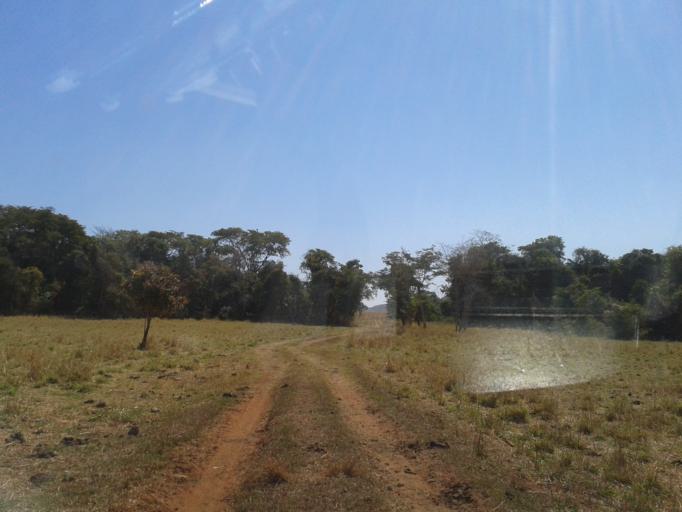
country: BR
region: Minas Gerais
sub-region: Santa Vitoria
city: Santa Vitoria
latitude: -19.0759
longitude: -50.0340
